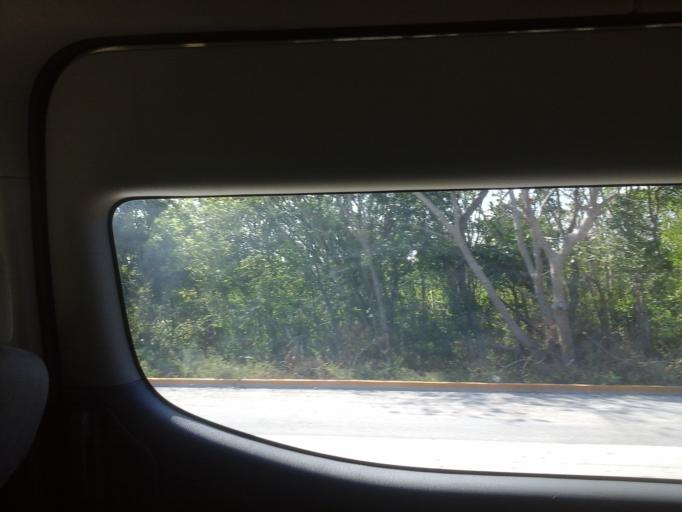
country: MX
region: Quintana Roo
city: Playa del Carmen
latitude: 20.7226
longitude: -87.0110
